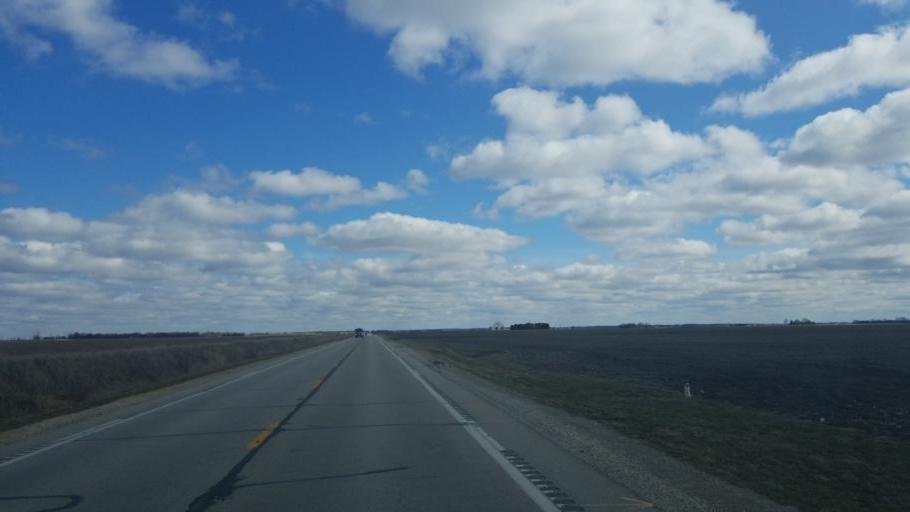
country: US
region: Illinois
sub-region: Douglas County
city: Villa Grove
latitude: 39.7919
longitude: -88.1177
